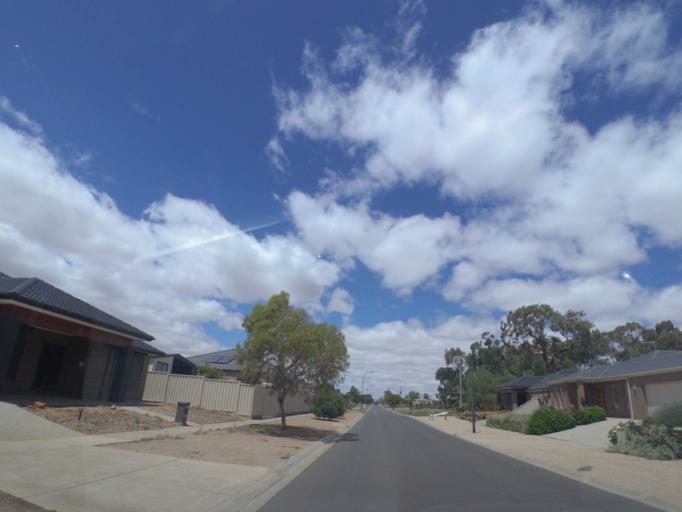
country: AU
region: Victoria
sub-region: Moorabool
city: Bacchus Marsh
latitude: -37.6502
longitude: 144.4437
